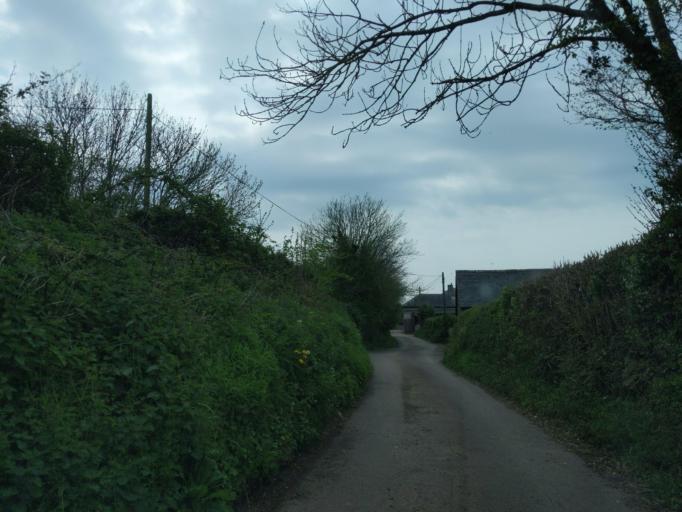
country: GB
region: England
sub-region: Borough of Torbay
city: Brixham
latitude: 50.3894
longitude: -3.5486
